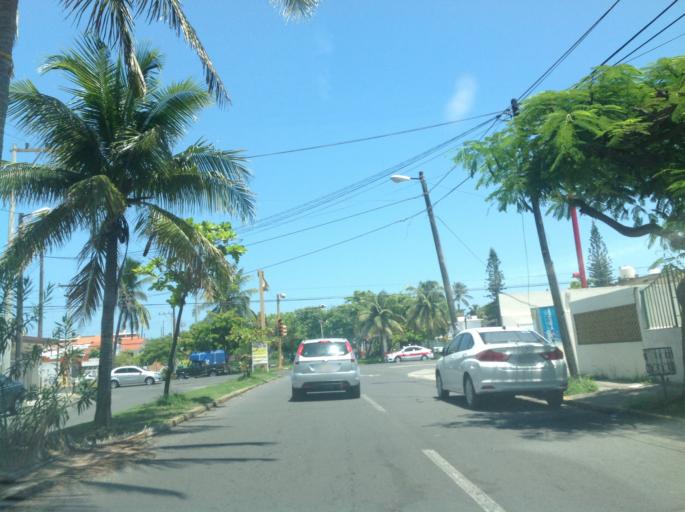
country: MX
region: Veracruz
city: Veracruz
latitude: 19.1581
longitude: -96.1356
